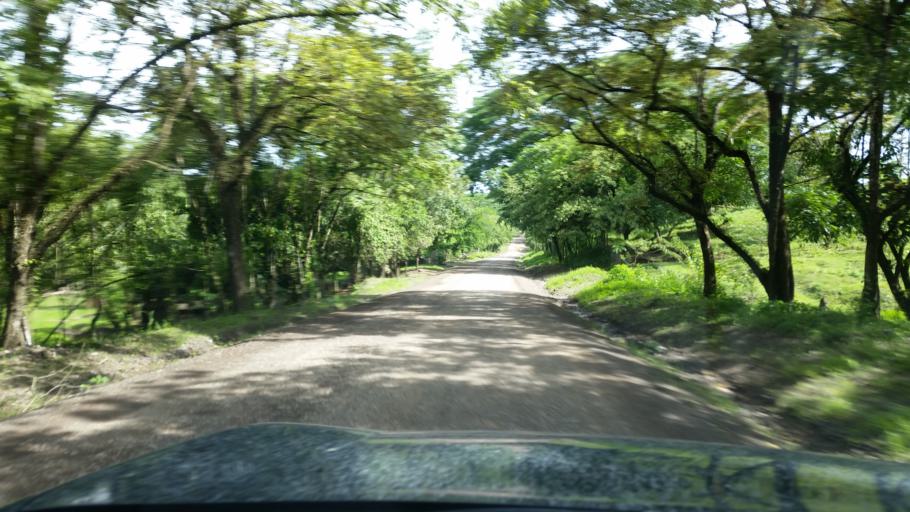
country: NI
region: Atlantico Norte (RAAN)
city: Siuna
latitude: 13.6641
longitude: -84.7924
